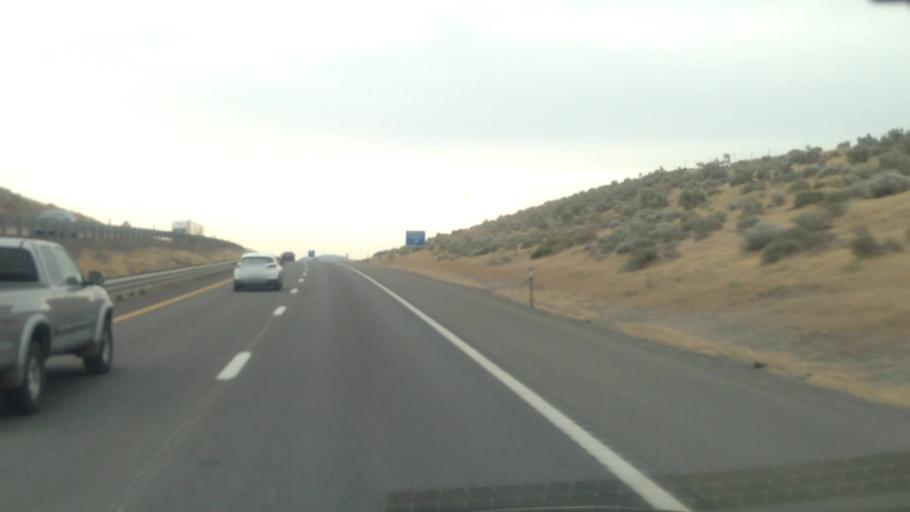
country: US
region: Nevada
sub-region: Washoe County
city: Spanish Springs
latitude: 39.5490
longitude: -119.5780
